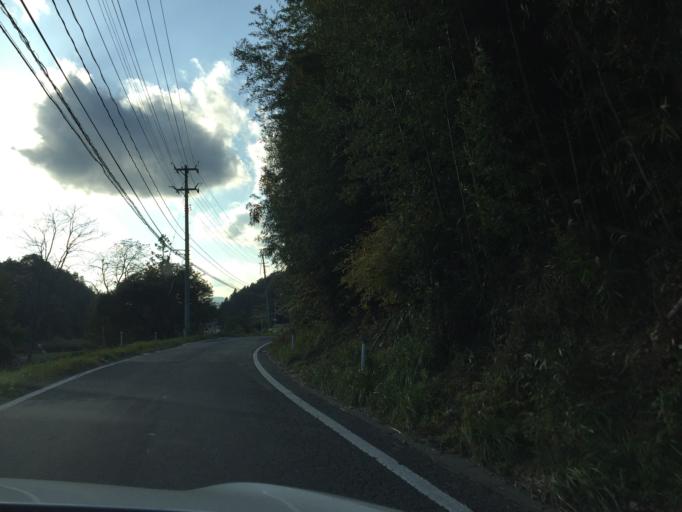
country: JP
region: Fukushima
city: Funehikimachi-funehiki
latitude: 37.2915
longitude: 140.6598
